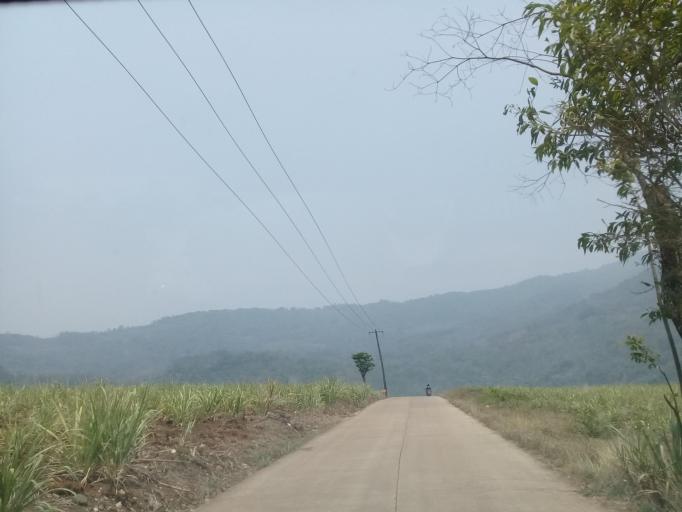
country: MX
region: Veracruz
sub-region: Tezonapa
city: Laguna Chica (Pueblo Nuevo)
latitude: 18.5686
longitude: -96.7224
